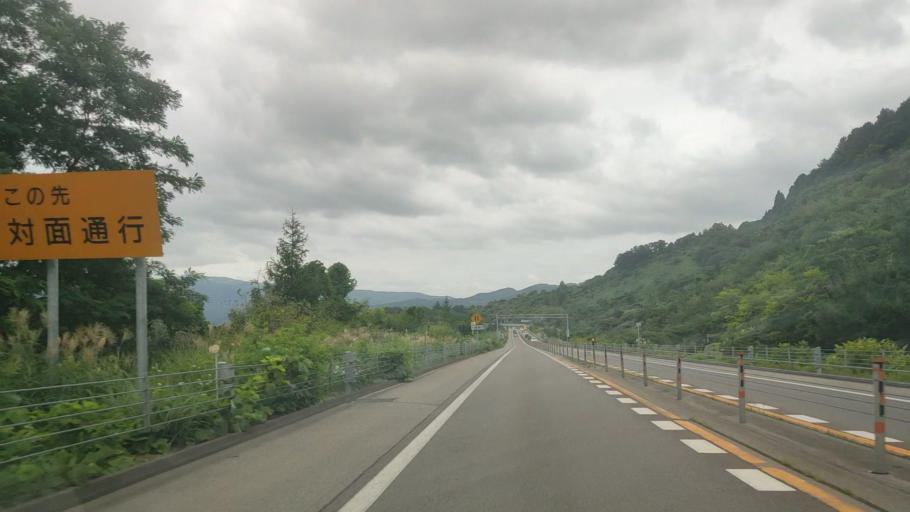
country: JP
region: Hokkaido
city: Nanae
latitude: 41.9099
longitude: 140.6941
